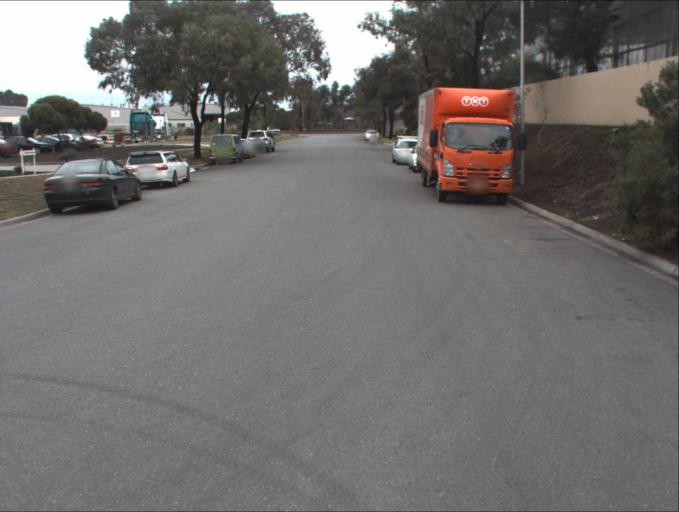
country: AU
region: South Australia
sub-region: Port Adelaide Enfield
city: Blair Athol
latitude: -34.8446
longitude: 138.5721
